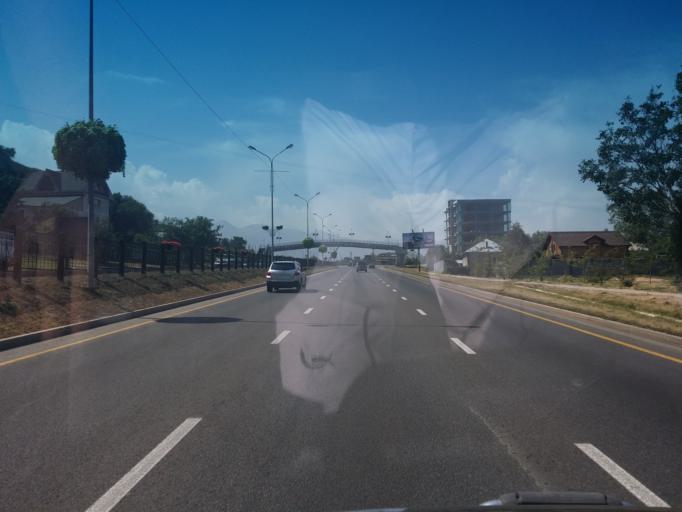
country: KZ
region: Almaty Qalasy
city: Almaty
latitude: 43.2401
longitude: 76.9728
